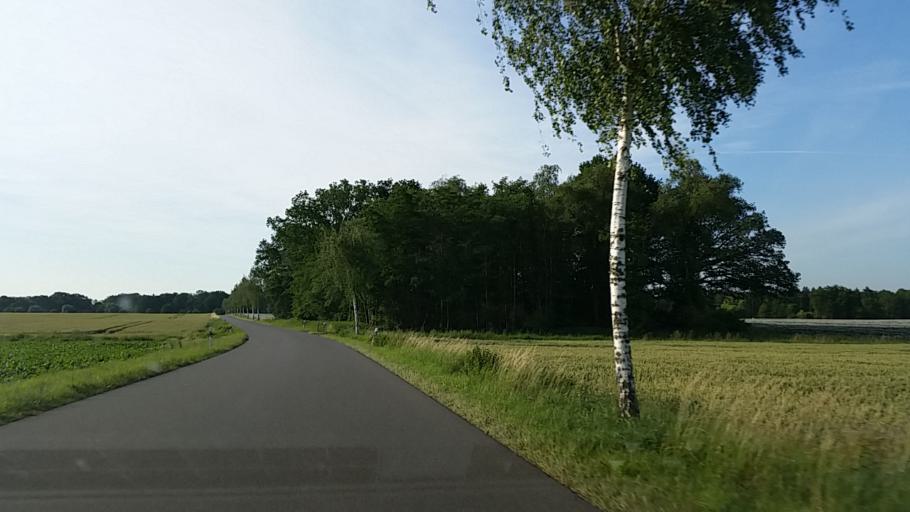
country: DE
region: Lower Saxony
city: Wieren
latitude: 52.9175
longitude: 10.6534
